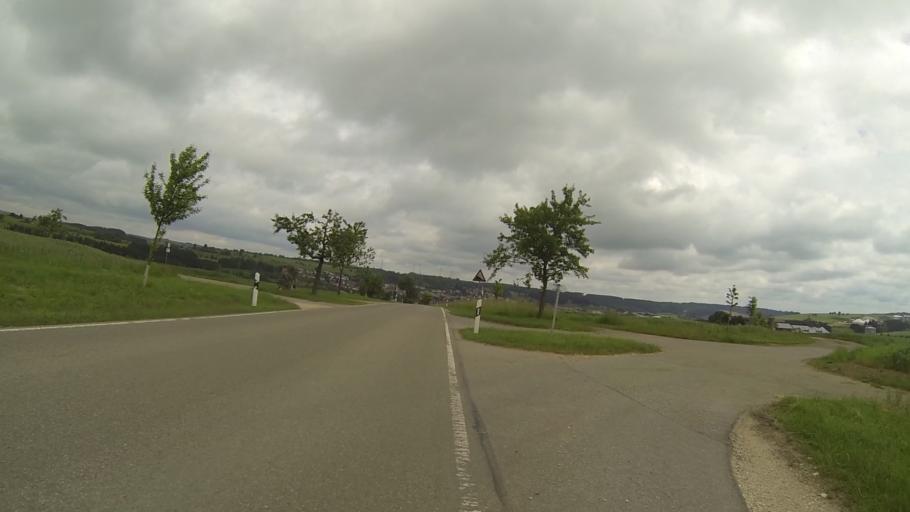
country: DE
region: Baden-Wuerttemberg
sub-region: Regierungsbezirk Stuttgart
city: Bohmenkirch
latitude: 48.6633
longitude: 9.9763
